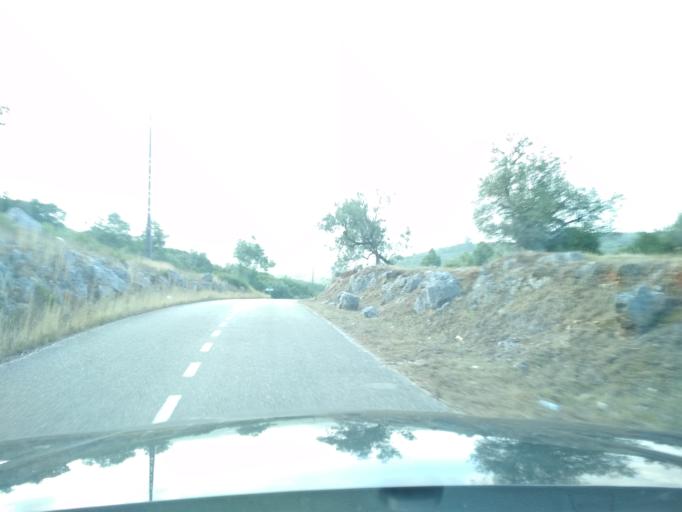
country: PT
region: Coimbra
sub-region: Condeixa-A-Nova
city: Condeixa-a-Nova
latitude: 40.0773
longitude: -8.5061
